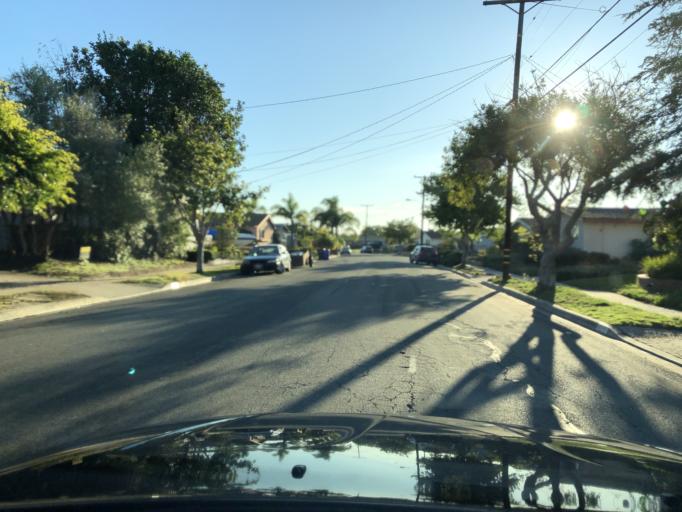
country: US
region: California
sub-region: San Diego County
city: La Jolla
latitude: 32.8177
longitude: -117.1950
